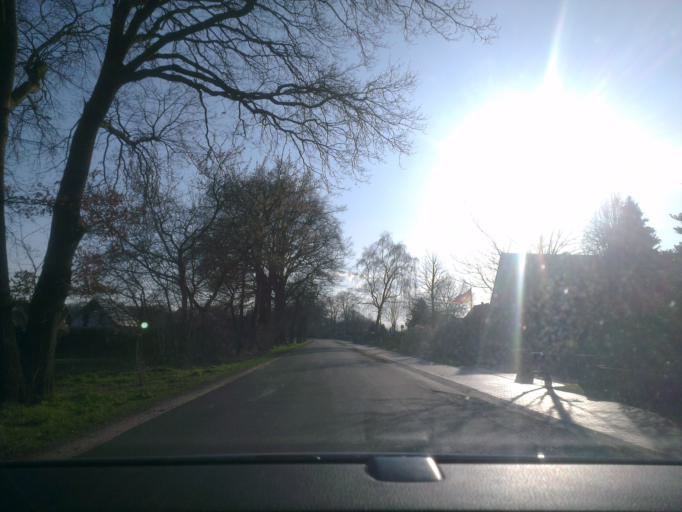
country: DE
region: Lower Saxony
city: Lastrup
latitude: 52.7547
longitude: 7.8211
